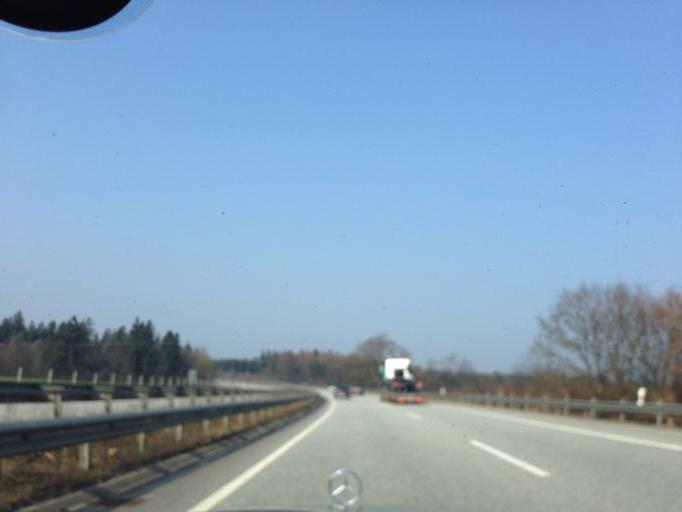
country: DE
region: Schleswig-Holstein
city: Daldorf
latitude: 54.0245
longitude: 10.2452
